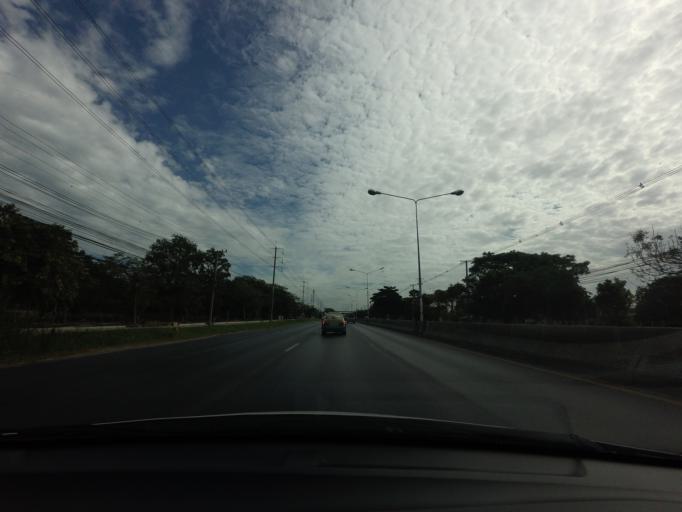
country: TH
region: Pathum Thani
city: Thanyaburi
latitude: 14.0166
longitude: 100.7255
